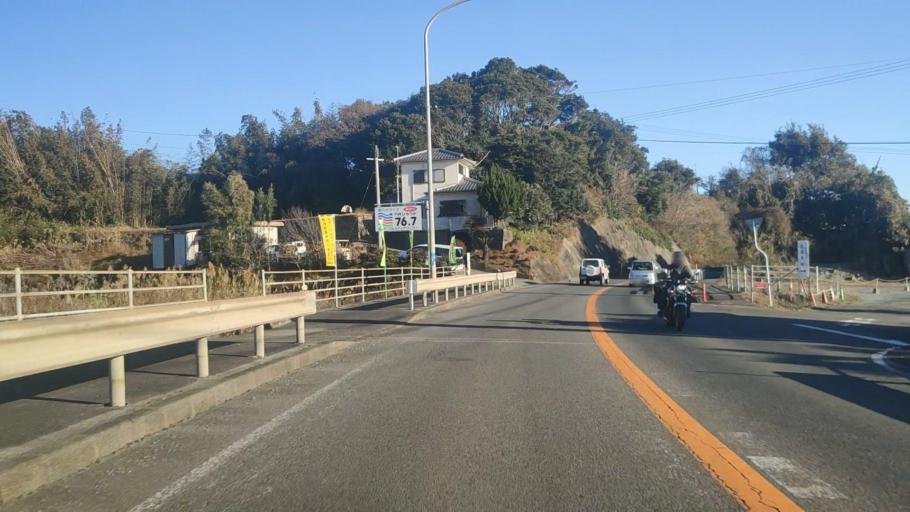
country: JP
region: Miyazaki
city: Nobeoka
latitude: 32.3643
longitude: 131.6234
